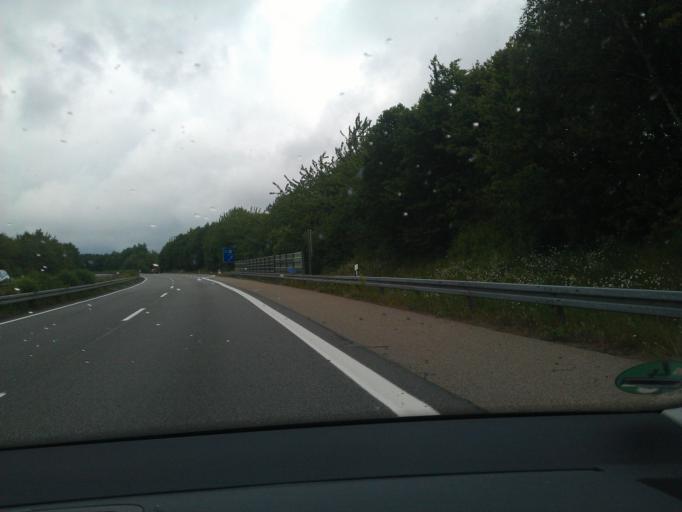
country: DE
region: Rheinland-Pfalz
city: Achtelsbach
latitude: 49.5930
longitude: 7.0547
